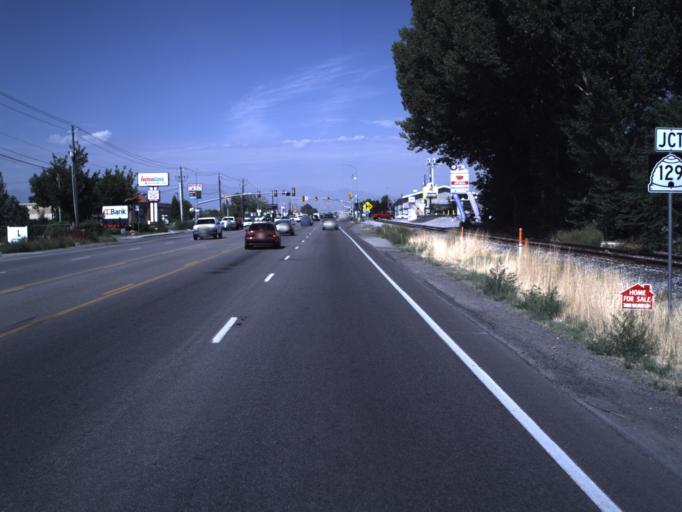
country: US
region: Utah
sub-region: Utah County
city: Pleasant Grove
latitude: 40.3697
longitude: -111.7667
